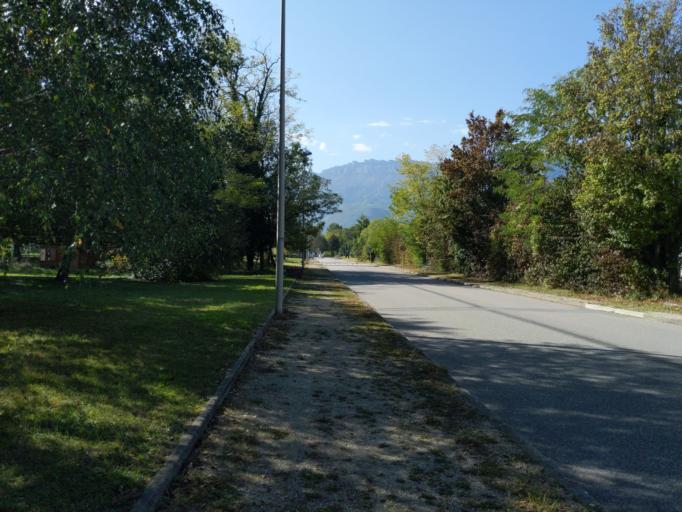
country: FR
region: Rhone-Alpes
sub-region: Departement de la Savoie
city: Montmelian
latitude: 45.4779
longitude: 6.0356
